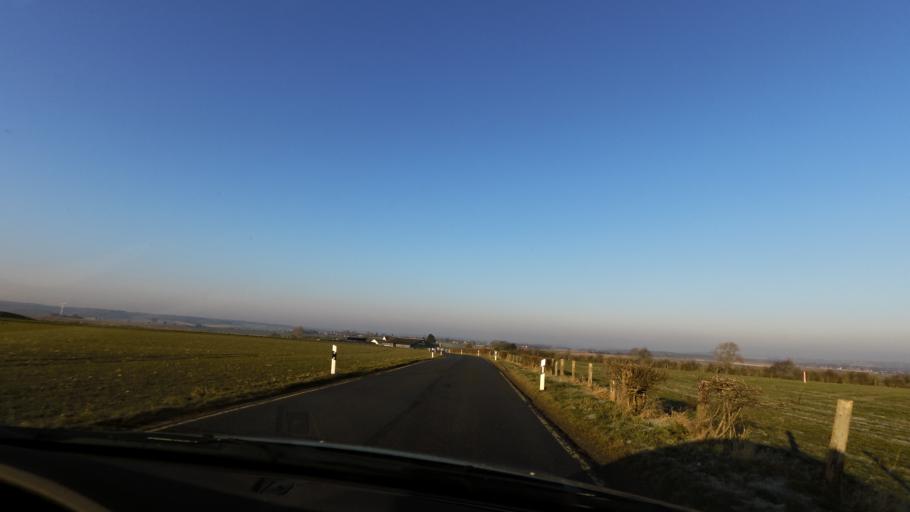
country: NL
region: Limburg
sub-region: Gemeente Vaals
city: Vaals
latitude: 50.8005
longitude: 6.0248
